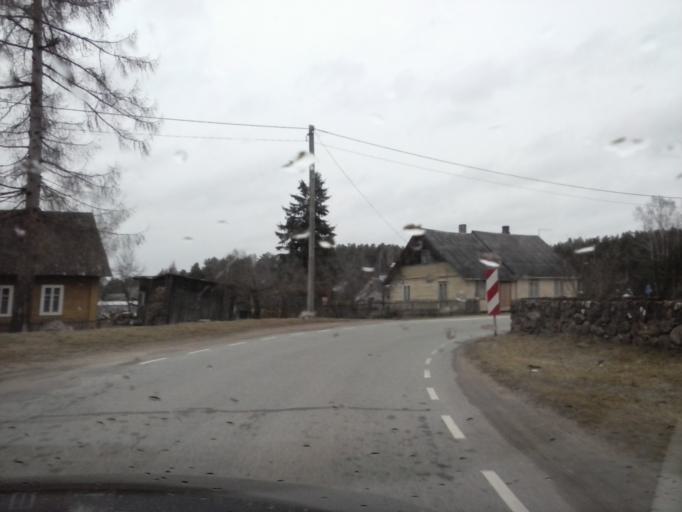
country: RU
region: Pskov
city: Pechory
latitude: 57.9603
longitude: 27.6291
